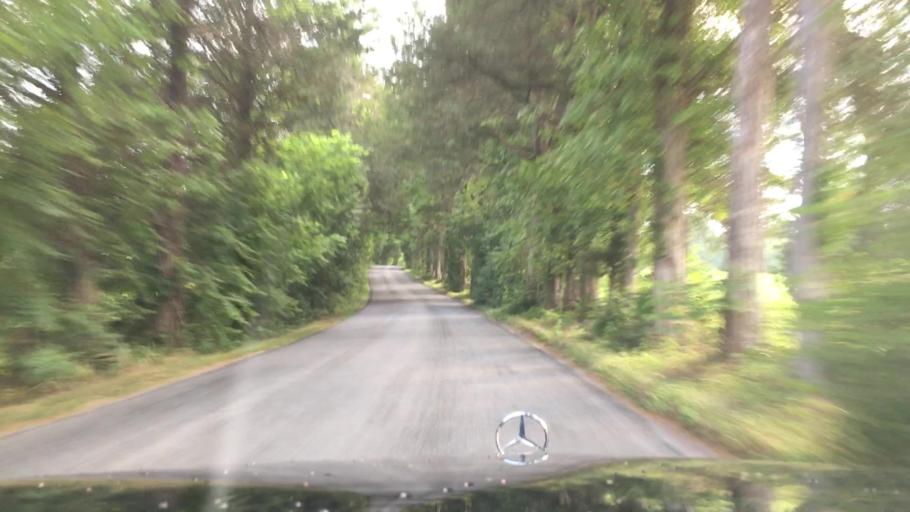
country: US
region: Virginia
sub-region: Campbell County
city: Timberlake
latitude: 37.2609
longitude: -79.3134
